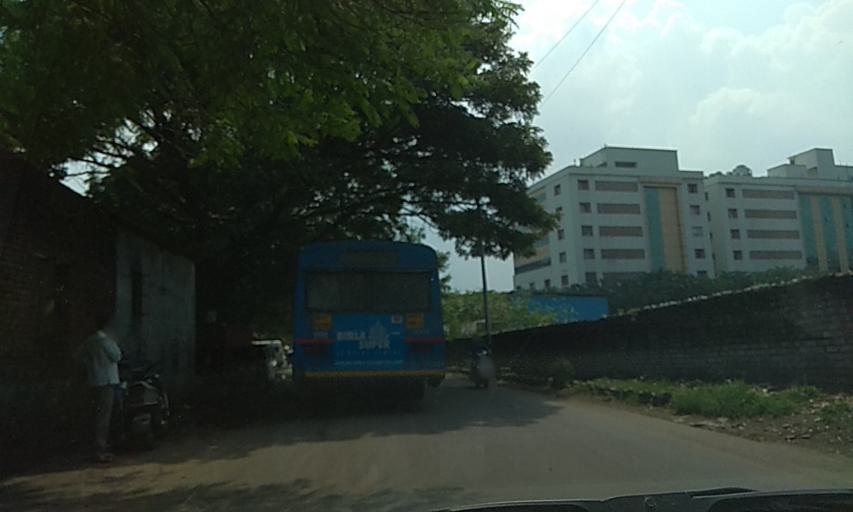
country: IN
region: Maharashtra
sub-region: Pune Division
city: Shivaji Nagar
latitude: 18.5385
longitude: 73.7939
